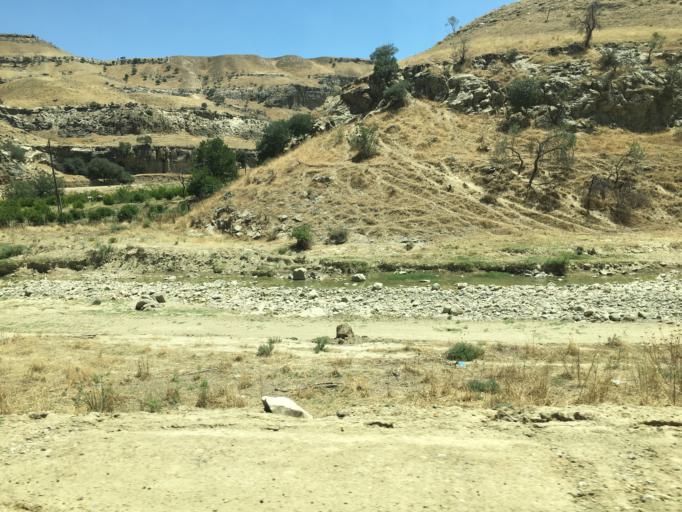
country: TM
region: Balkan
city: Magtymguly
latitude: 38.4204
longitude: 56.6880
